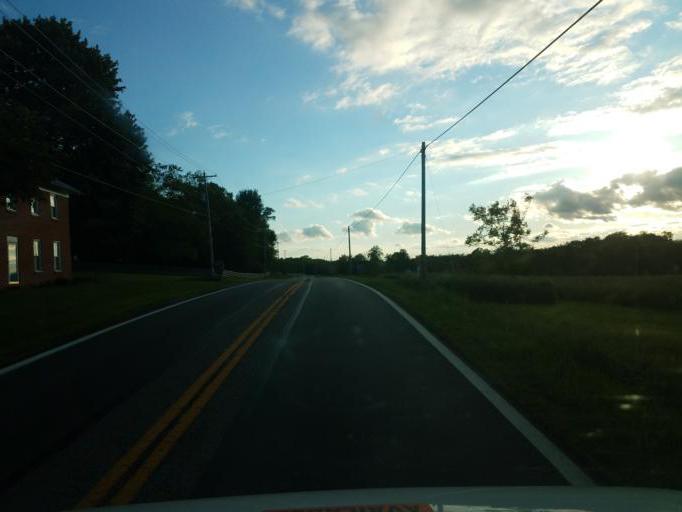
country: US
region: Ohio
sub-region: Knox County
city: Fredericktown
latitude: 40.4026
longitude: -82.6008
